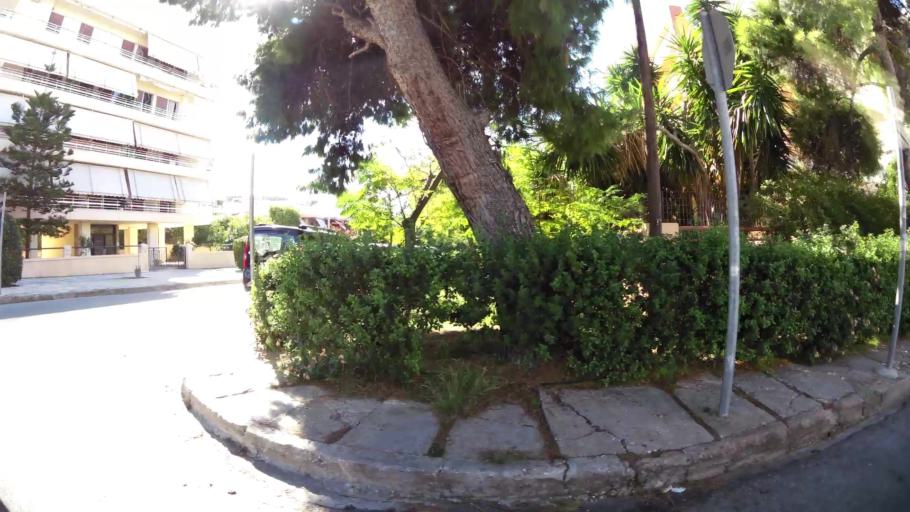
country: GR
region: Attica
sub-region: Nomarchia Athinas
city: Glyfada
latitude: 37.8758
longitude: 23.7586
